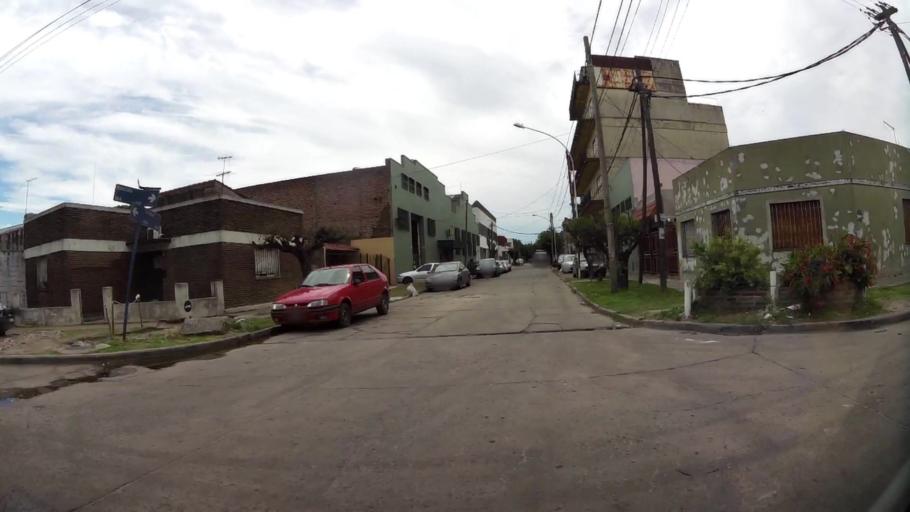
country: AR
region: Buenos Aires
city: San Justo
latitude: -34.6751
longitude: -58.5411
